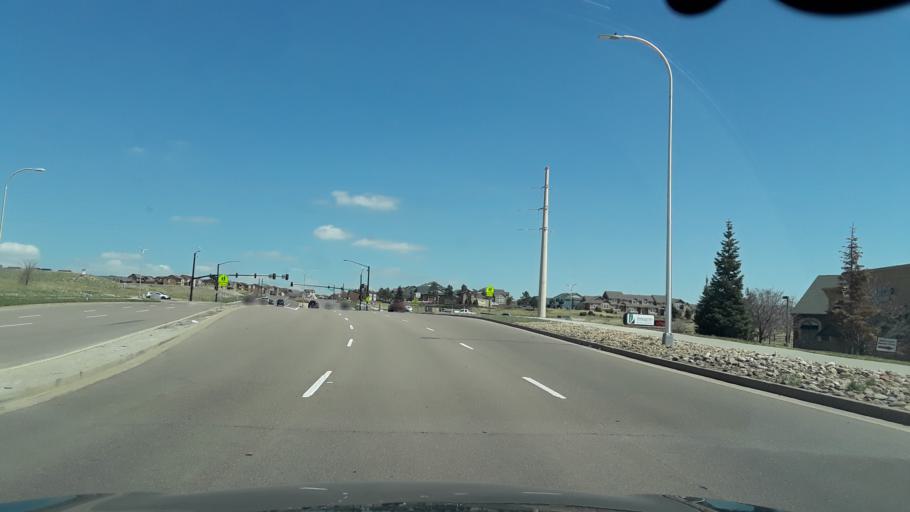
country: US
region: Colorado
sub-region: El Paso County
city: Black Forest
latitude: 38.9553
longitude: -104.7288
